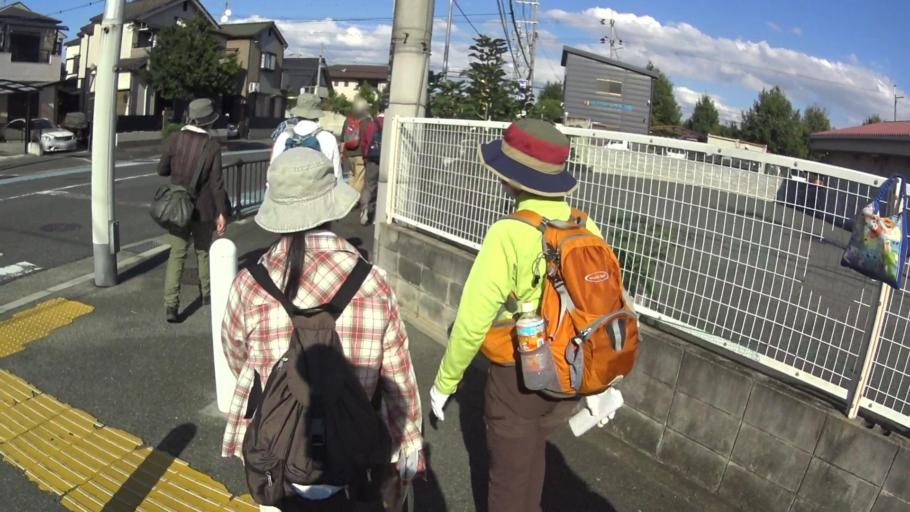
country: JP
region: Ehime
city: Kihoku-cho
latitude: 33.3912
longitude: 132.8456
